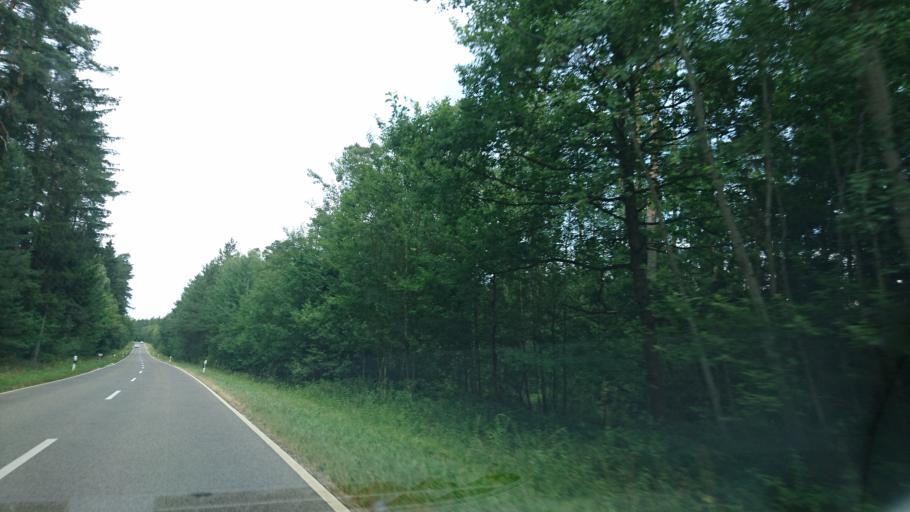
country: DE
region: Bavaria
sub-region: Regierungsbezirk Mittelfranken
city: Heideck
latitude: 49.1687
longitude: 11.1196
